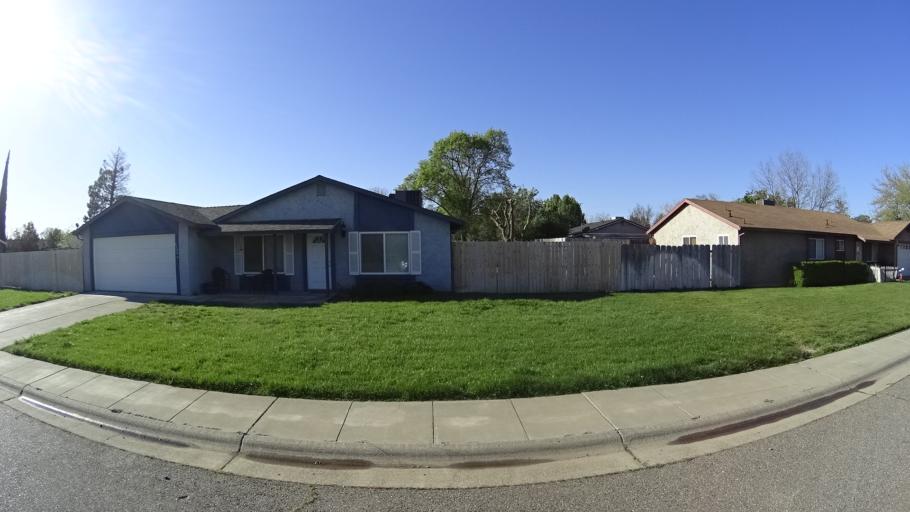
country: US
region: California
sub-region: Glenn County
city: Orland
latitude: 39.7605
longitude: -122.2218
